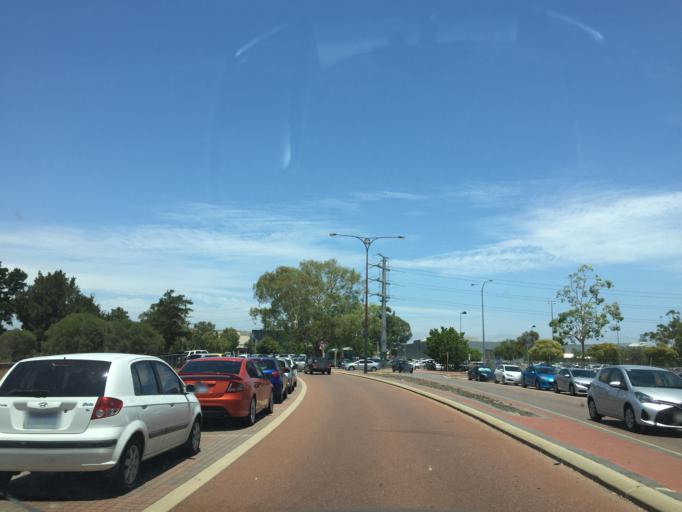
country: AU
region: Western Australia
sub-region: Canning
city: Cannington
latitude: -32.0170
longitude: 115.9422
